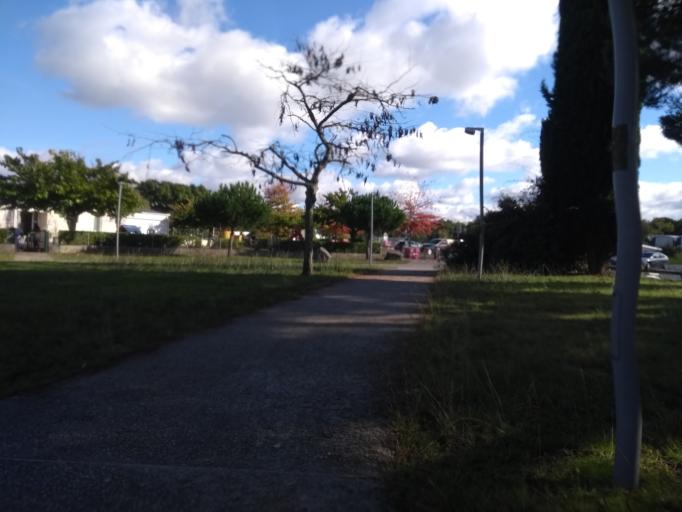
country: FR
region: Aquitaine
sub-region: Departement de la Gironde
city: Pessac
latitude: 44.7940
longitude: -0.6274
